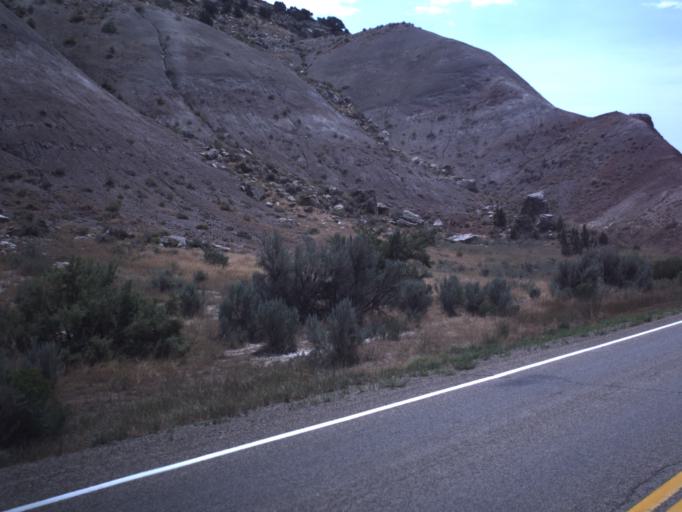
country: US
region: Utah
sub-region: Uintah County
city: Vernal
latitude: 40.5280
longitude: -109.5223
